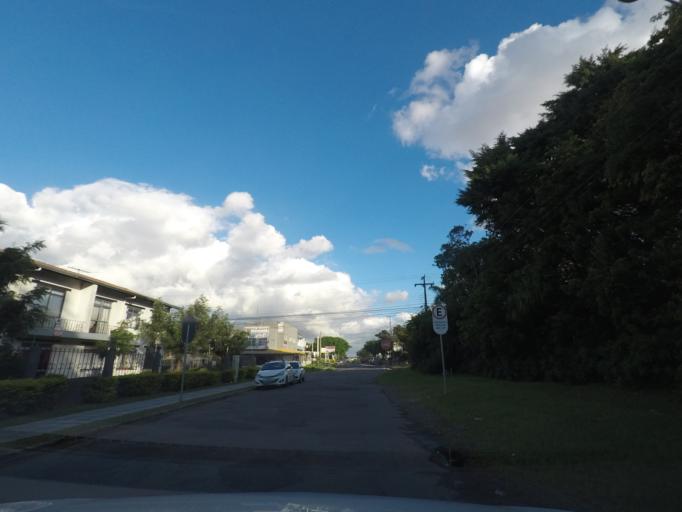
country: BR
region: Parana
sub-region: Curitiba
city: Curitiba
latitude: -25.4859
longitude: -49.2605
